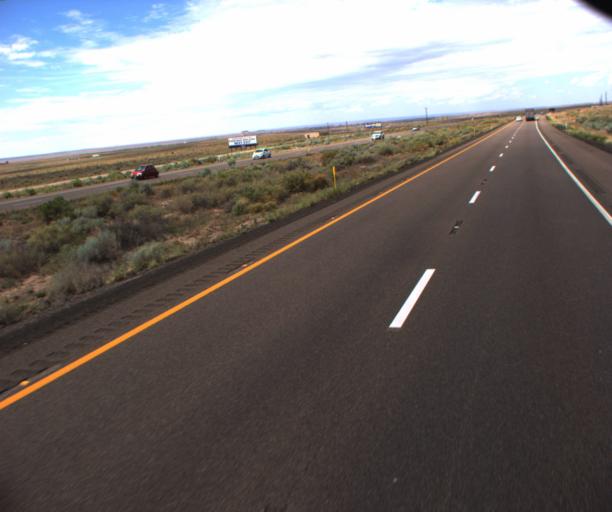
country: US
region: Arizona
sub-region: Navajo County
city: Holbrook
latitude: 35.0047
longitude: -109.8831
